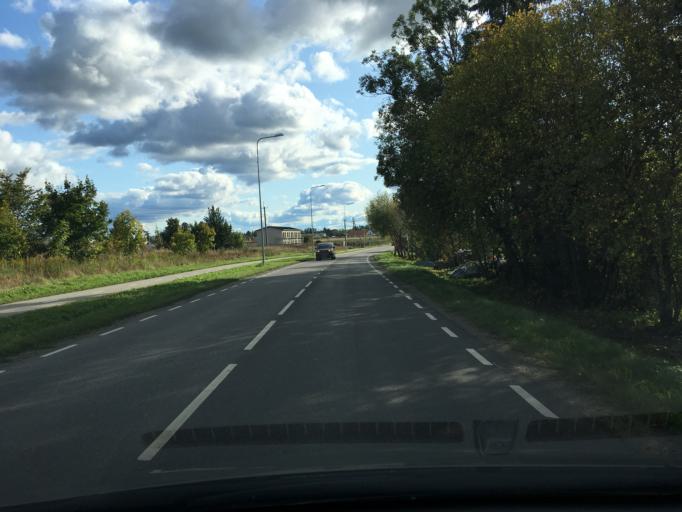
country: EE
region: Harju
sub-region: Joelaehtme vald
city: Loo
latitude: 59.4109
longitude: 24.9477
